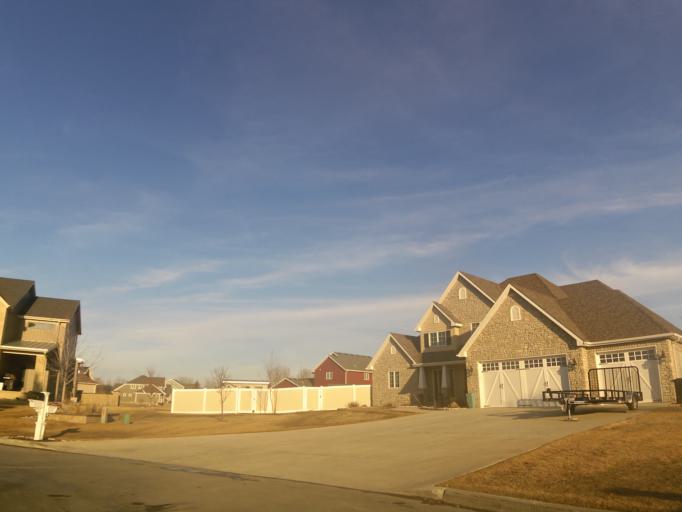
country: US
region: North Dakota
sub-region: Grand Forks County
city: Grand Forks
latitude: 47.8683
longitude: -97.0366
